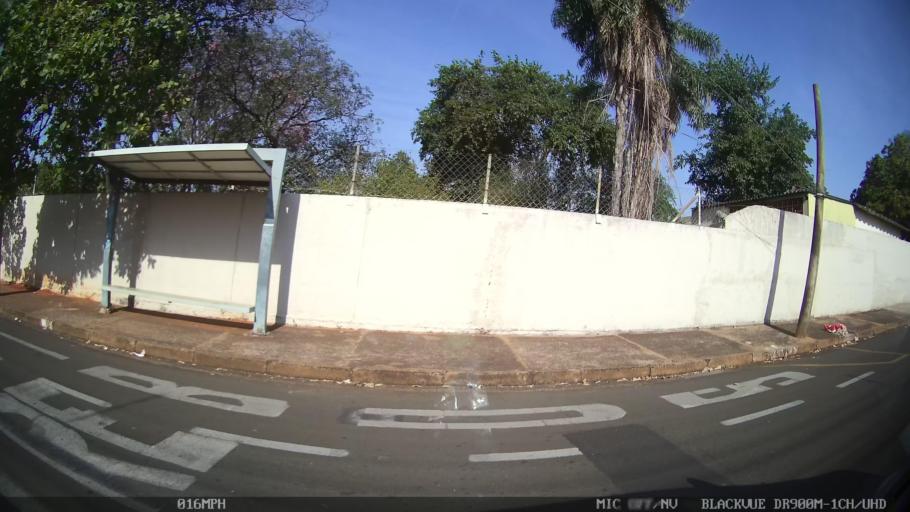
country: BR
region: Sao Paulo
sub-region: Sao Jose Do Rio Preto
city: Sao Jose do Rio Preto
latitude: -20.7918
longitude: -49.3802
